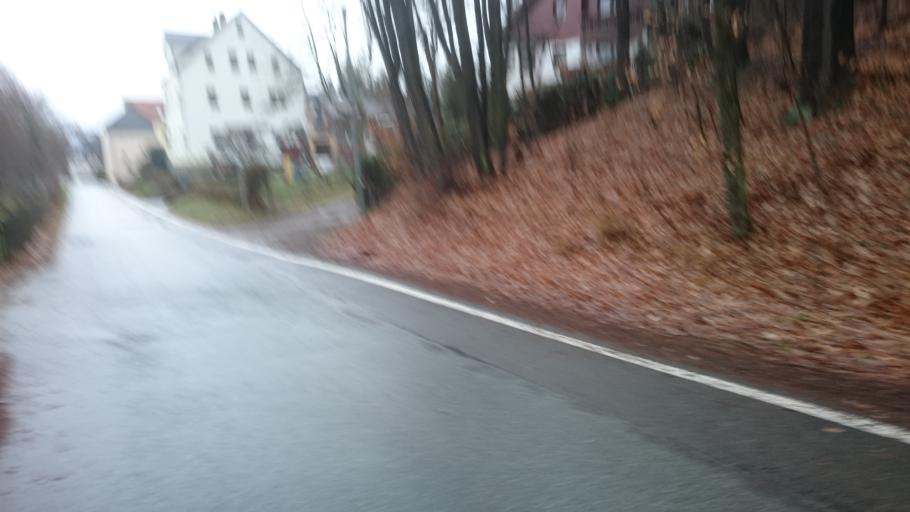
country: DE
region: Saxony
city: Zwickau
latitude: 50.7571
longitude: 12.5114
